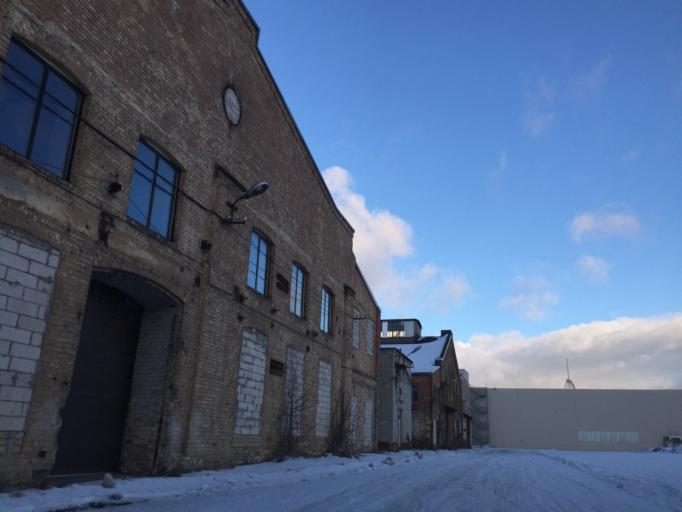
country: LV
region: Riga
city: Riga
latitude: 56.9733
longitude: 24.1601
